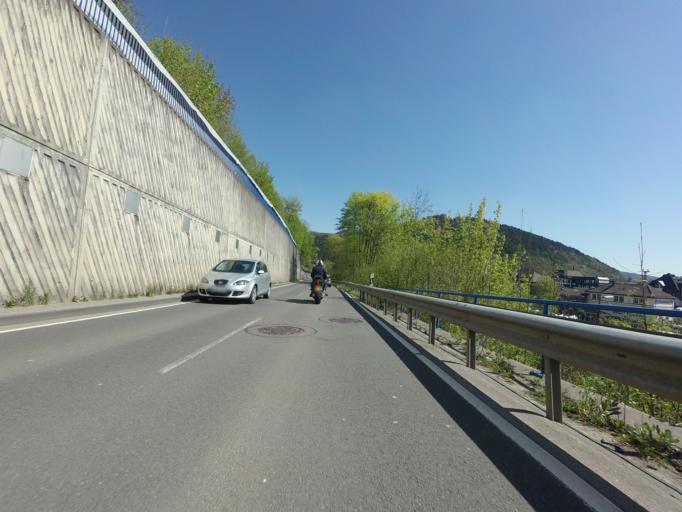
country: DE
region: North Rhine-Westphalia
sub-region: Regierungsbezirk Arnsberg
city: Lennestadt
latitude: 51.1043
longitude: 8.0705
